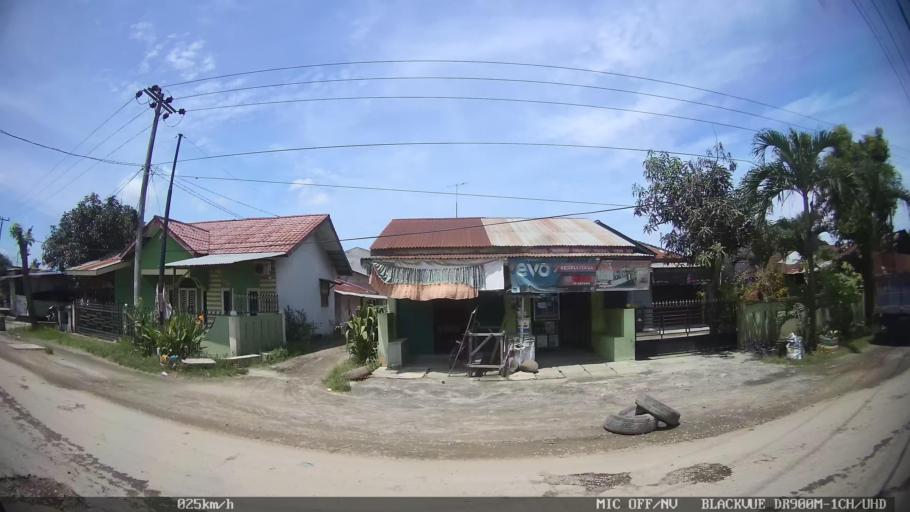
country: ID
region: North Sumatra
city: Perbaungan
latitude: 3.5431
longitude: 98.8825
